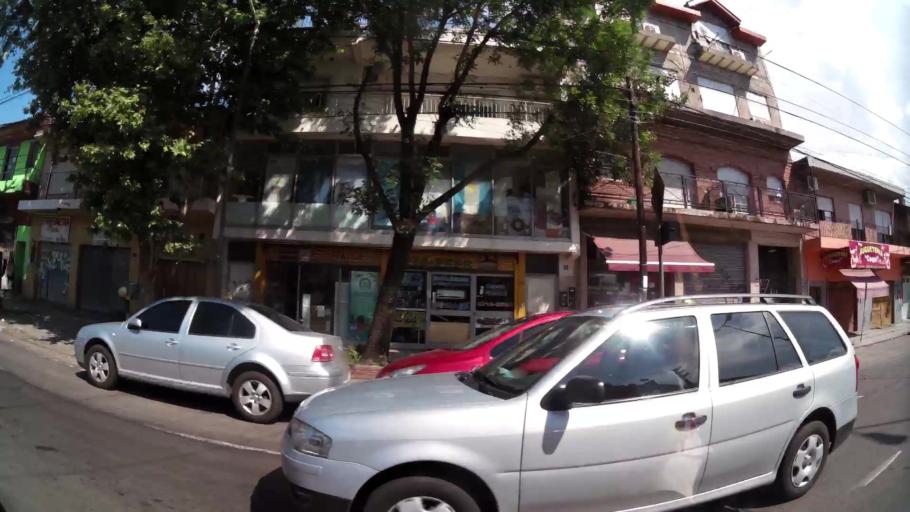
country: AR
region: Buenos Aires
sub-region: Partido de Tigre
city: Tigre
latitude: -34.4625
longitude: -58.5761
